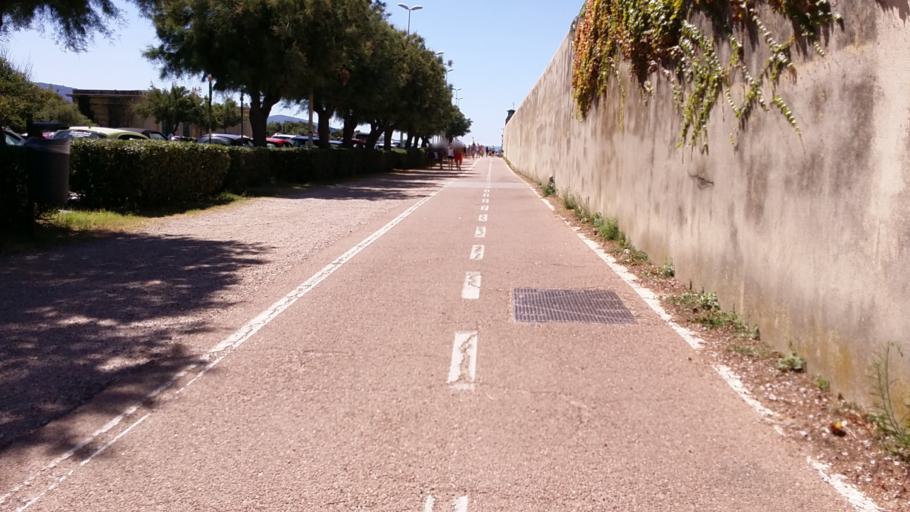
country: IT
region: Tuscany
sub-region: Provincia di Livorno
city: Livorno
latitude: 43.5236
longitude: 10.3107
